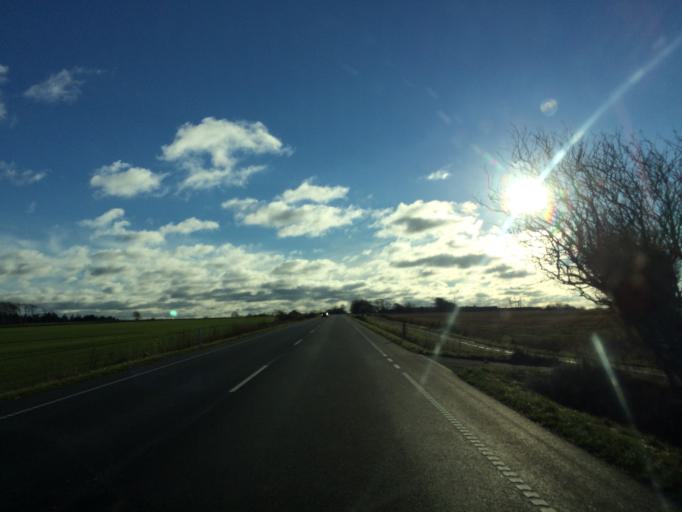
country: DK
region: Central Jutland
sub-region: Herning Kommune
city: Kibaek
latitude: 56.0207
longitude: 8.8516
